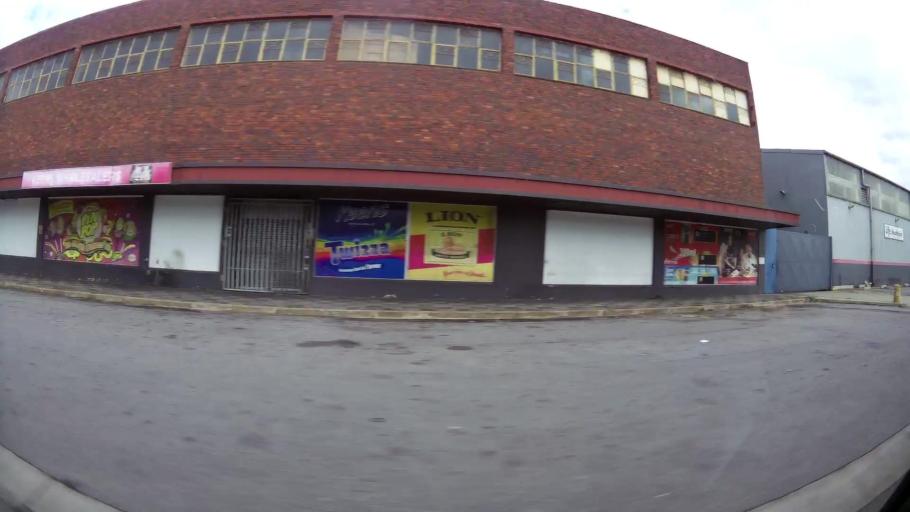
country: ZA
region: Eastern Cape
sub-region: Nelson Mandela Bay Metropolitan Municipality
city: Port Elizabeth
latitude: -33.9320
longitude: 25.5865
